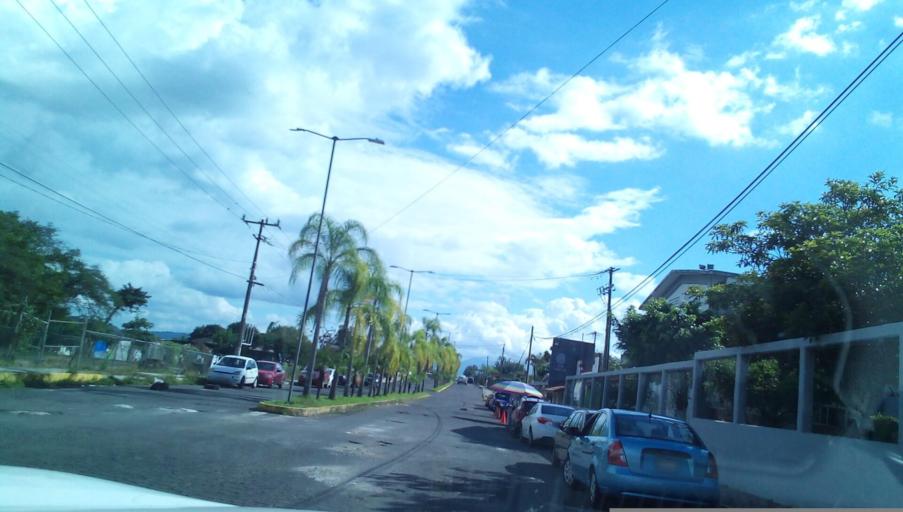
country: MX
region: Veracruz
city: Cordoba
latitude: 18.8923
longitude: -96.9212
